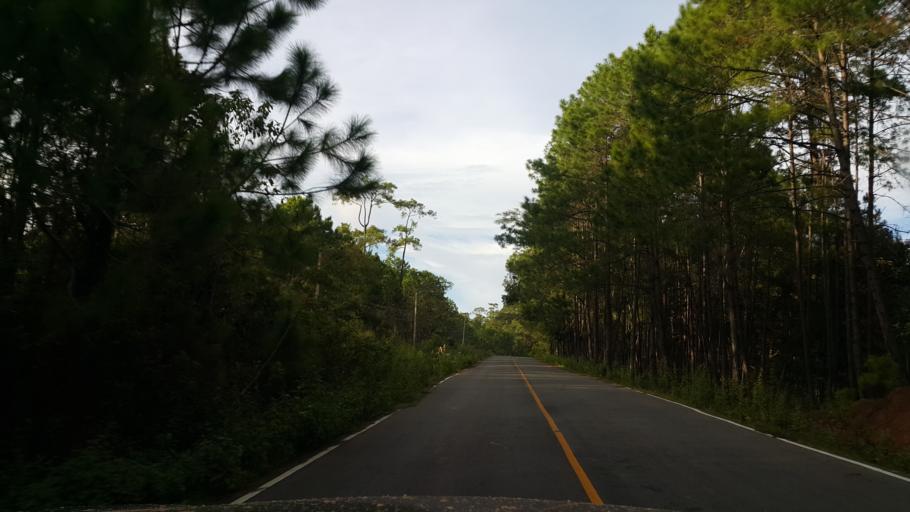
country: TH
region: Chiang Mai
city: Chaem Luang
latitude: 19.0836
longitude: 98.3380
